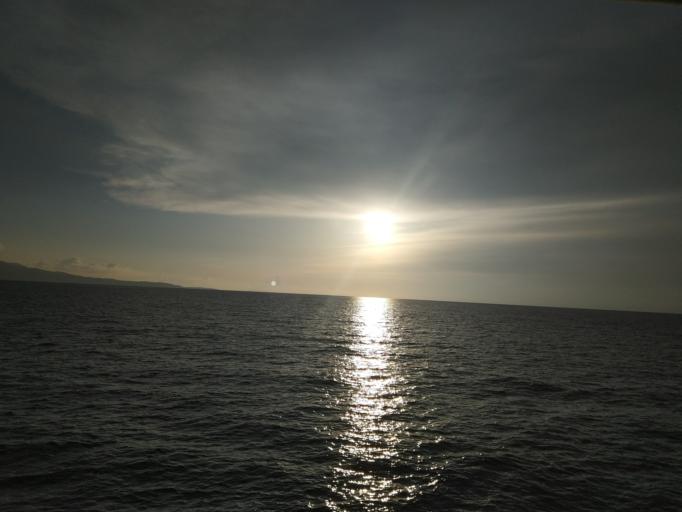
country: AL
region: Vlore
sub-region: Rrethi i Sarandes
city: Sarande
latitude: 39.8238
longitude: 19.9951
